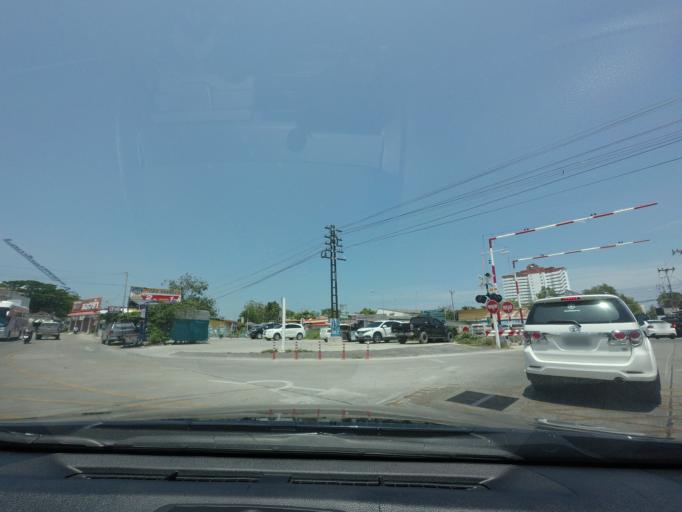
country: TH
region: Prachuap Khiri Khan
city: Hua Hin
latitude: 12.5611
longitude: 99.9560
